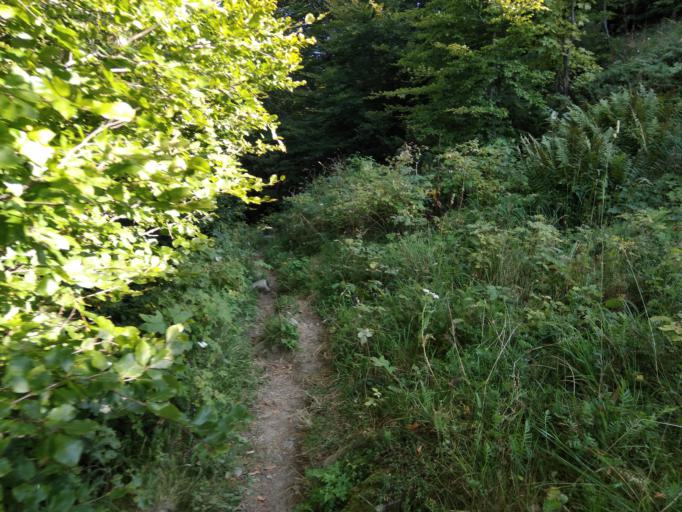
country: BG
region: Stara Zagora
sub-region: Obshtina Pavel Banya
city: Asen
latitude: 42.7614
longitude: 25.1117
